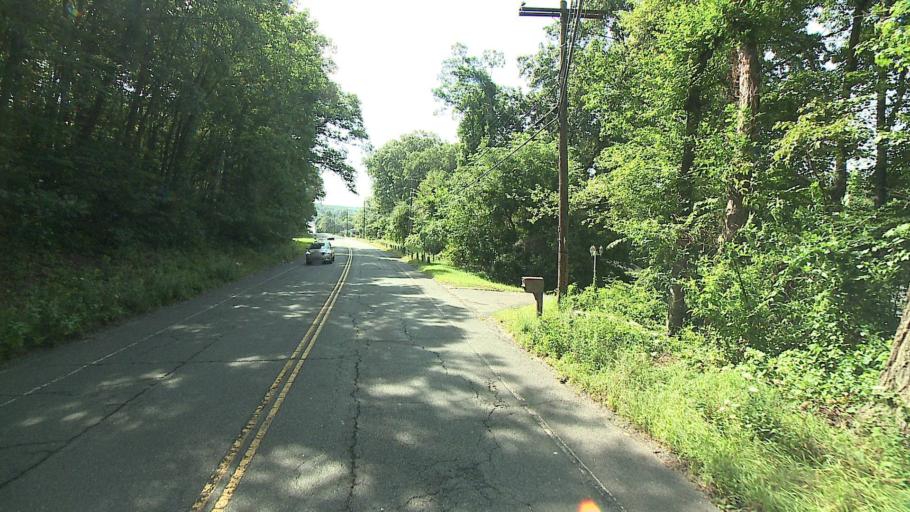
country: US
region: New York
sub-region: Putnam County
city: Putnam Lake
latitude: 41.4708
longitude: -73.4919
